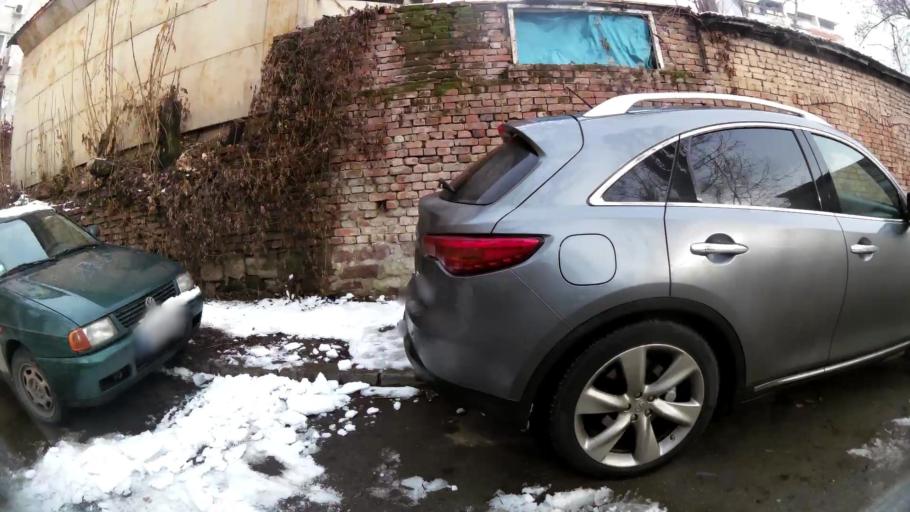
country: BG
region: Sofia-Capital
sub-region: Stolichna Obshtina
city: Sofia
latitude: 42.7080
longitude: 23.3065
